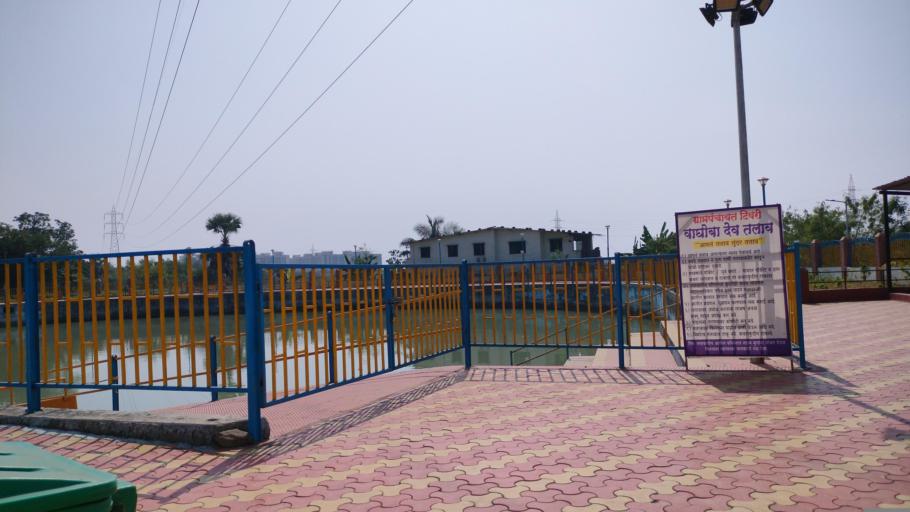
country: IN
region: Maharashtra
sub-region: Thane
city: Bhayandar
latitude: 19.3727
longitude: 72.8659
